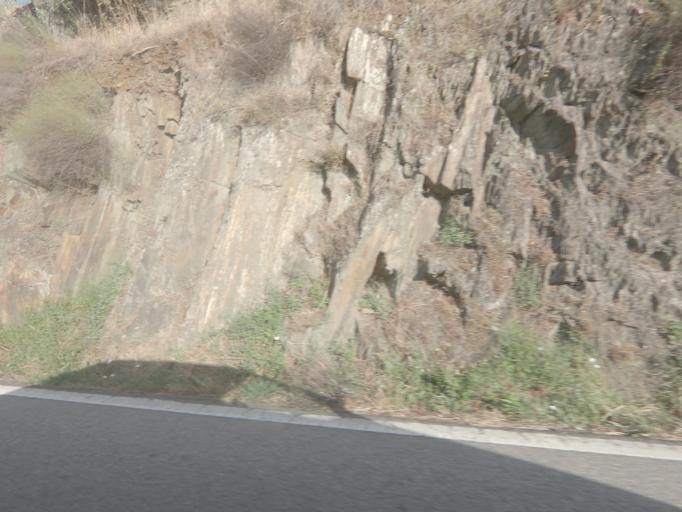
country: PT
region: Viseu
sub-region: Tabuaco
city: Tabuaco
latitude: 41.1715
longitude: -7.5556
